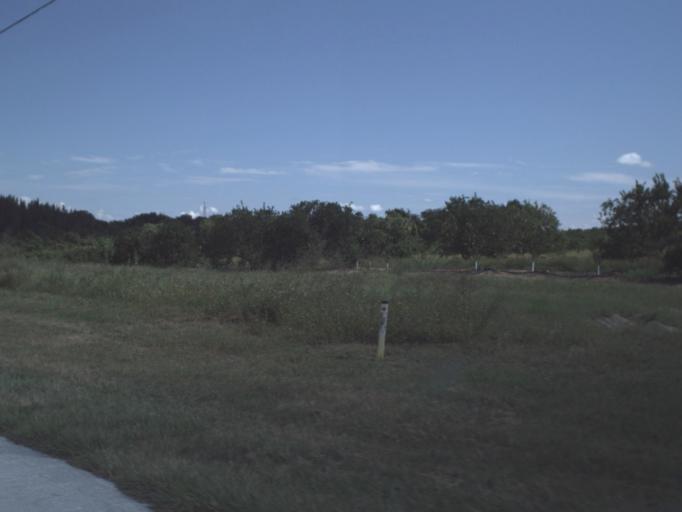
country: US
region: Florida
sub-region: Polk County
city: Lake Hamilton
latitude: 28.0368
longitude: -81.6198
